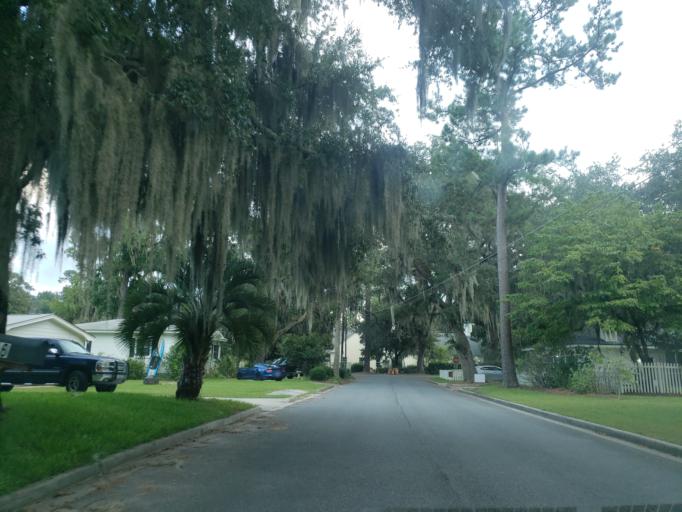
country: US
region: Georgia
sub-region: Chatham County
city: Isle of Hope
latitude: 31.9843
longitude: -81.0583
